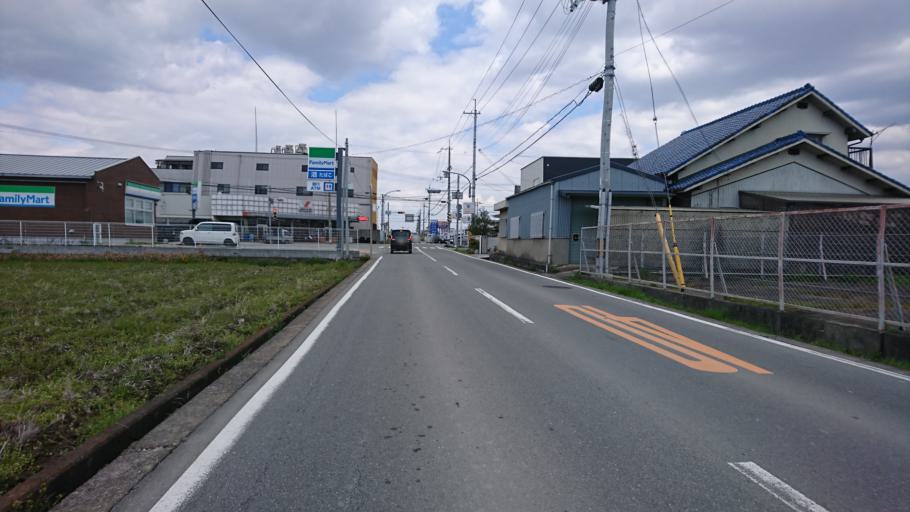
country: JP
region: Hyogo
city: Miki
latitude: 34.7461
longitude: 134.9354
